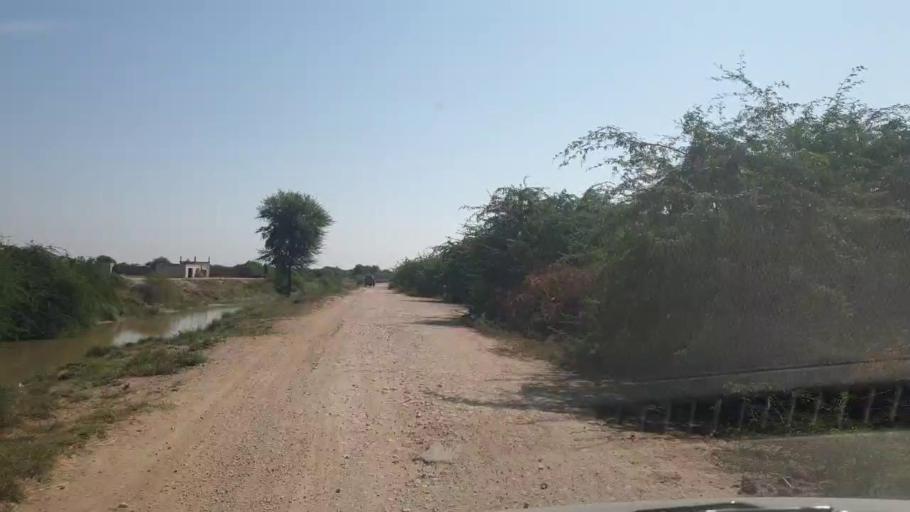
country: PK
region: Sindh
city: Digri
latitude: 24.9430
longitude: 69.1584
